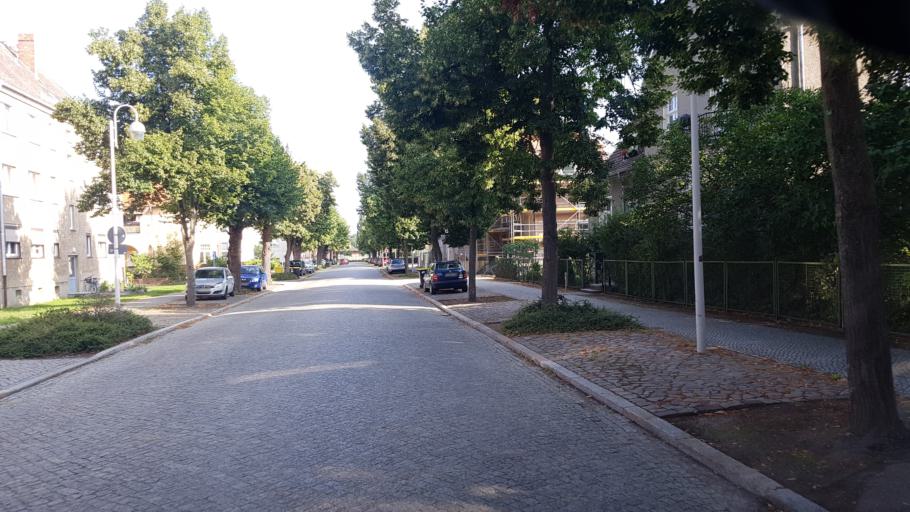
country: DE
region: Brandenburg
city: Luckau
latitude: 51.8550
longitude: 13.7144
